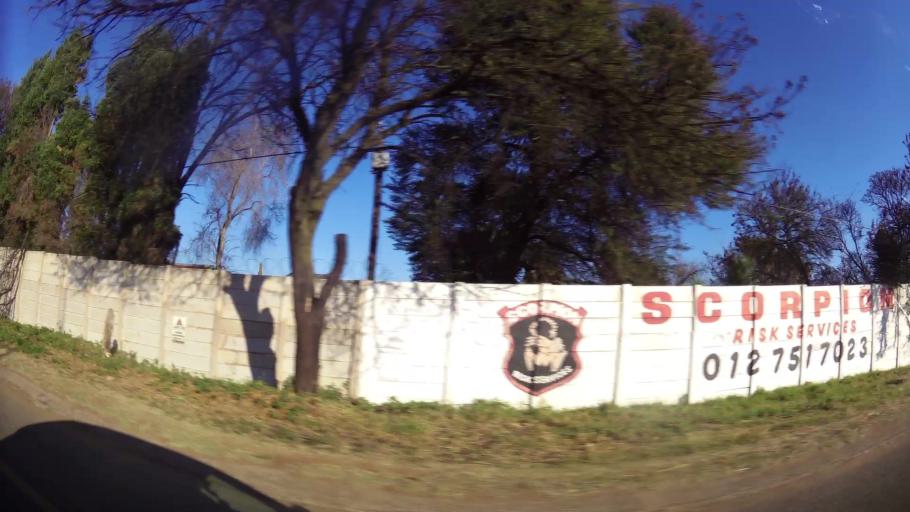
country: ZA
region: Gauteng
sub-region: City of Tshwane Metropolitan Municipality
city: Centurion
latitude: -25.8687
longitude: 28.1476
